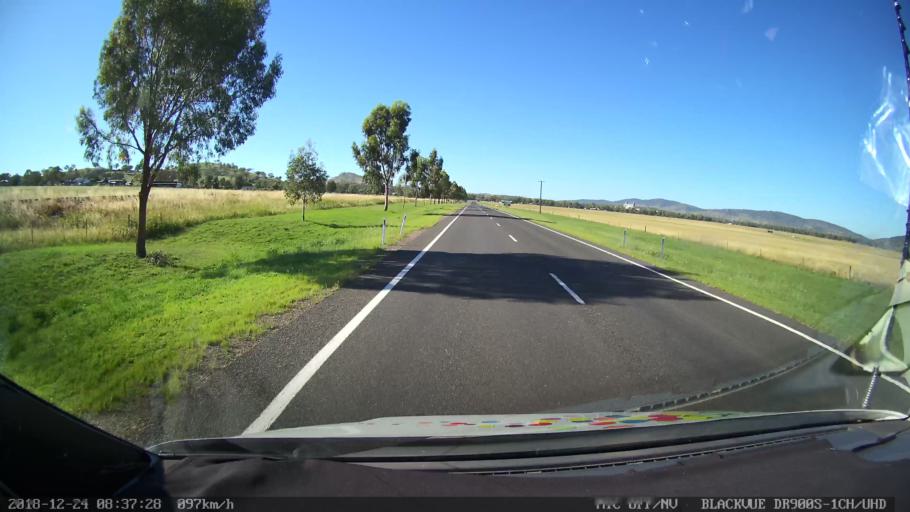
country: AU
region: New South Wales
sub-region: Liverpool Plains
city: Quirindi
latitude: -31.3292
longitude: 150.6488
